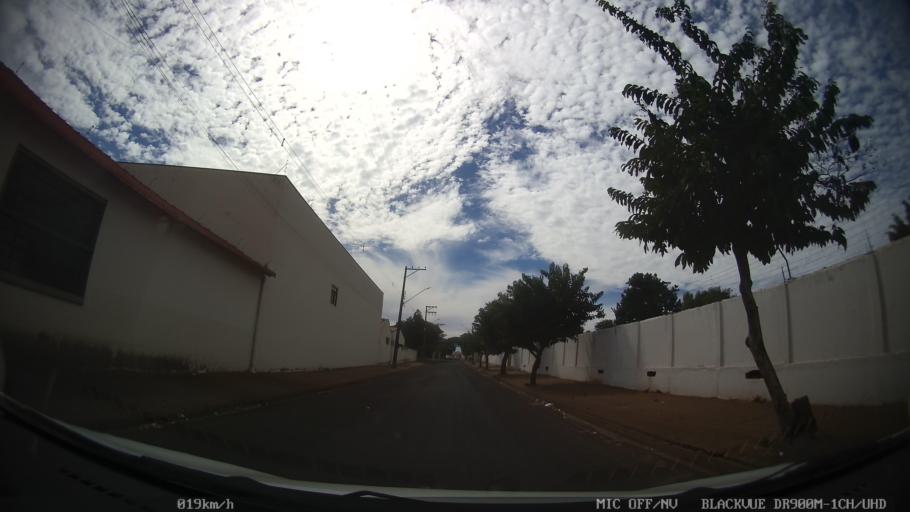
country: BR
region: Sao Paulo
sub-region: Catanduva
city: Catanduva
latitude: -21.1538
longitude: -48.9713
